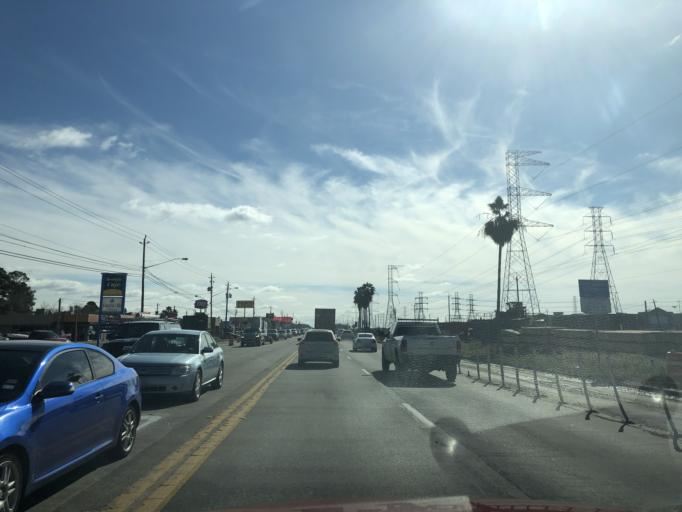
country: US
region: Texas
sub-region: Galveston County
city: Kemah
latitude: 29.5380
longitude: -95.0181
